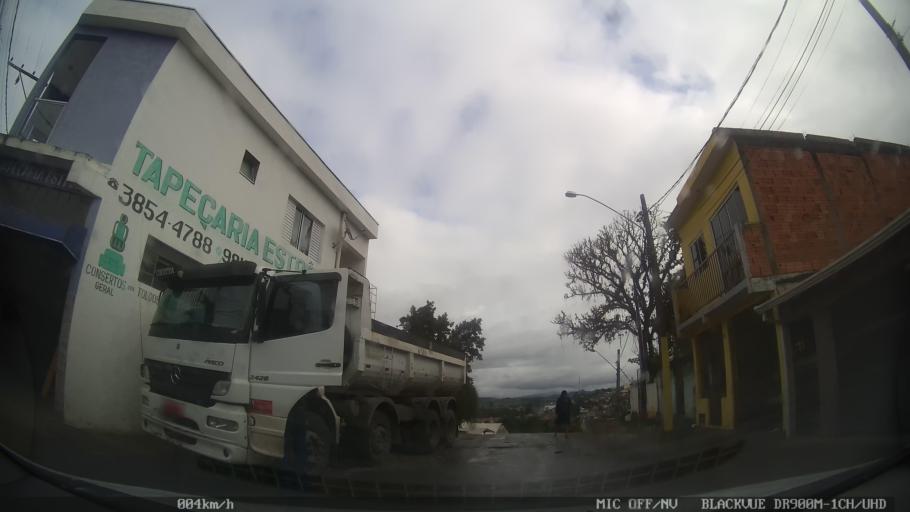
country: BR
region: Sao Paulo
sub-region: Cajati
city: Cajati
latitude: -24.7232
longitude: -48.1002
